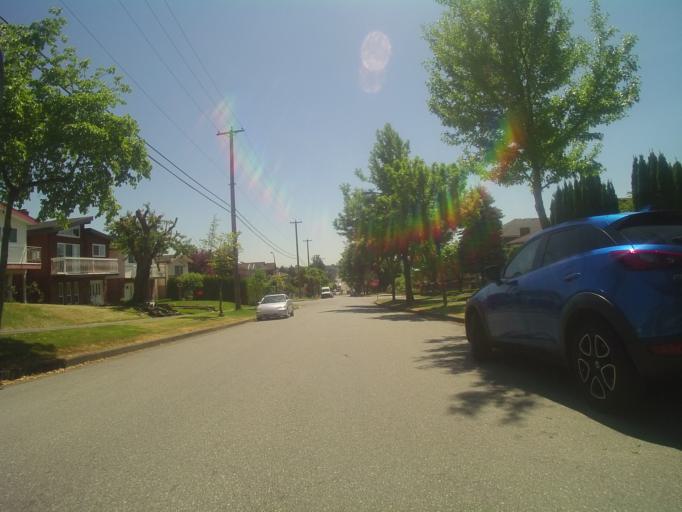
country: CA
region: British Columbia
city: Vancouver
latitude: 49.2148
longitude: -123.1064
